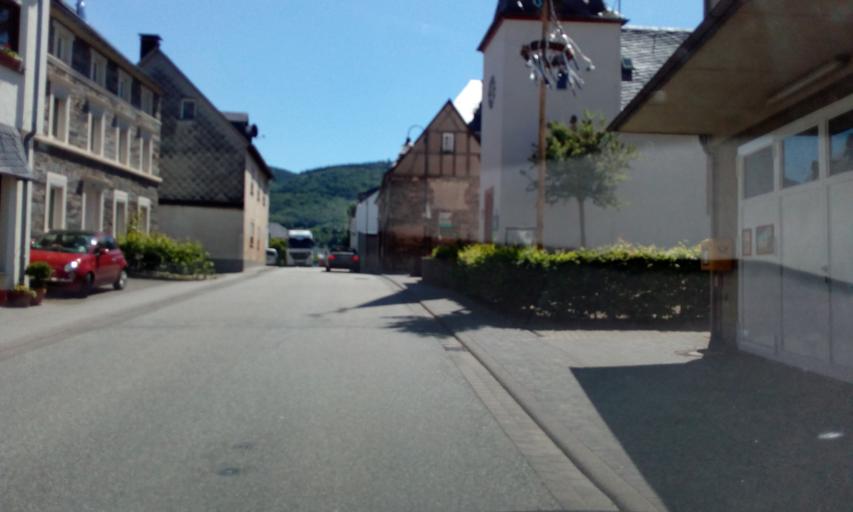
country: DE
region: Rheinland-Pfalz
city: Monzelfeld
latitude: 49.9093
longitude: 7.0421
